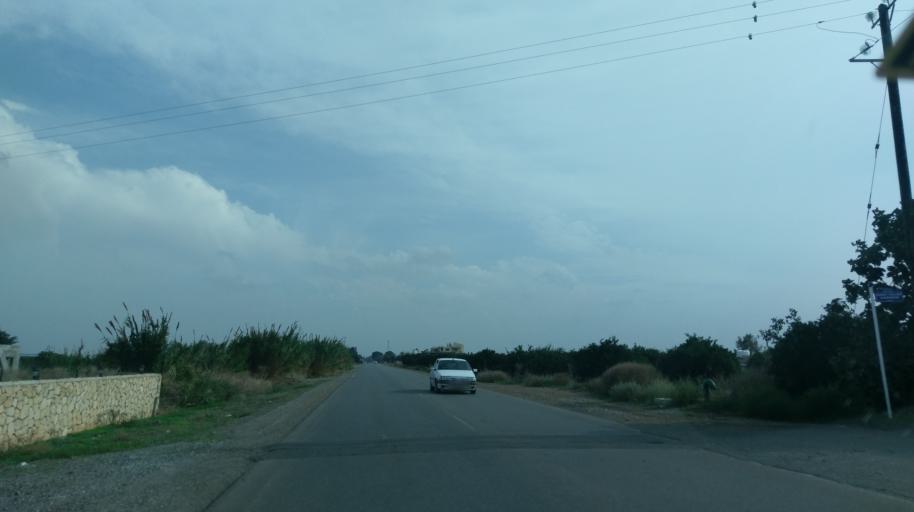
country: CY
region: Lefkosia
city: Morfou
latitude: 35.1817
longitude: 33.0246
